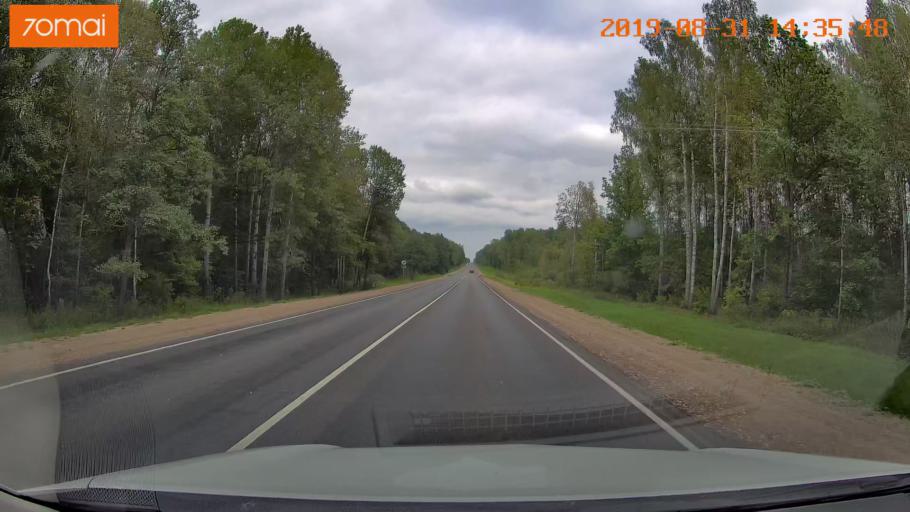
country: RU
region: Smolensk
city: Yekimovichi
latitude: 54.1653
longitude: 33.4640
